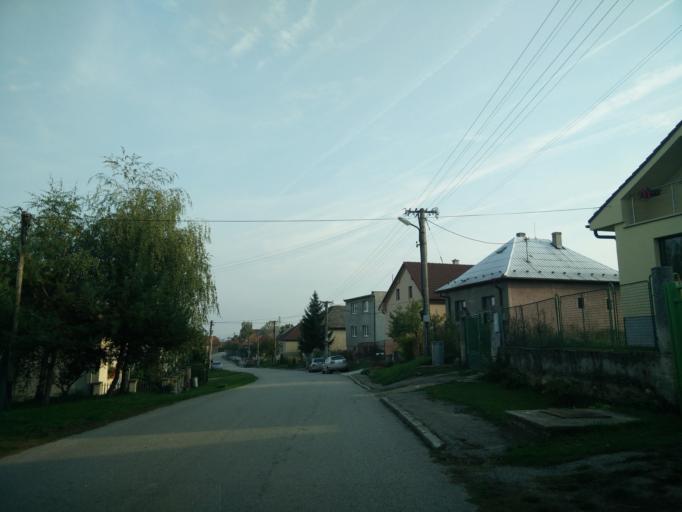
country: SK
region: Nitriansky
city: Banovce nad Bebravou
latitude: 48.7634
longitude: 18.1595
